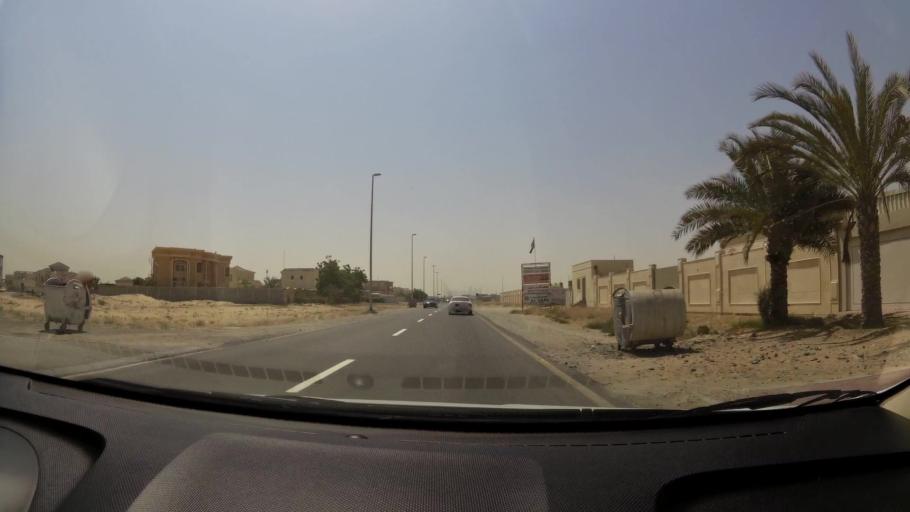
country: AE
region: Ajman
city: Ajman
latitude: 25.4173
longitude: 55.5183
